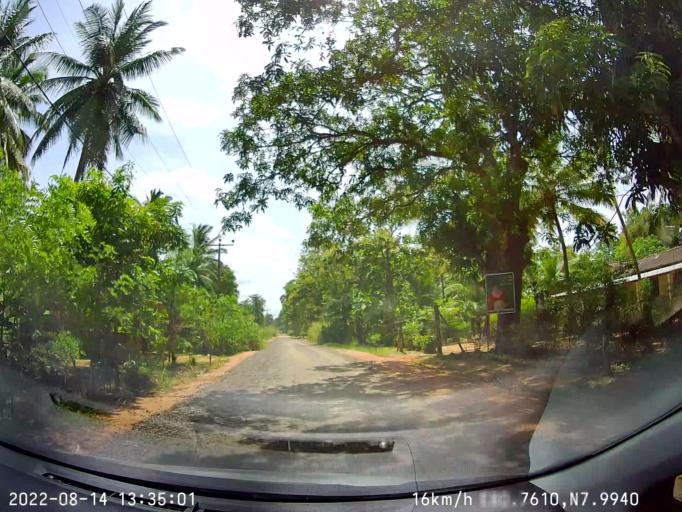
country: LK
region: Central
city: Sigiriya
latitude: 7.9942
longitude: 80.7609
